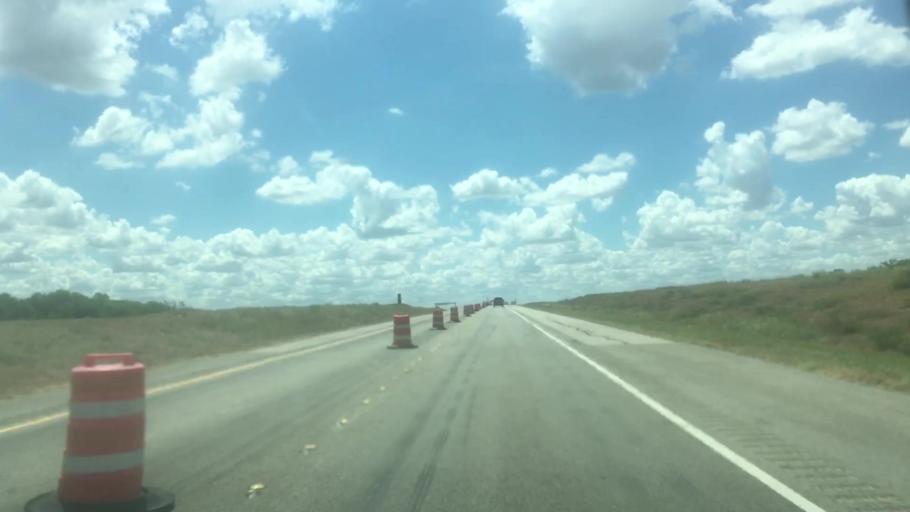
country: US
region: Texas
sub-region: Caldwell County
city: Martindale
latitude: 29.8205
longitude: -97.7549
